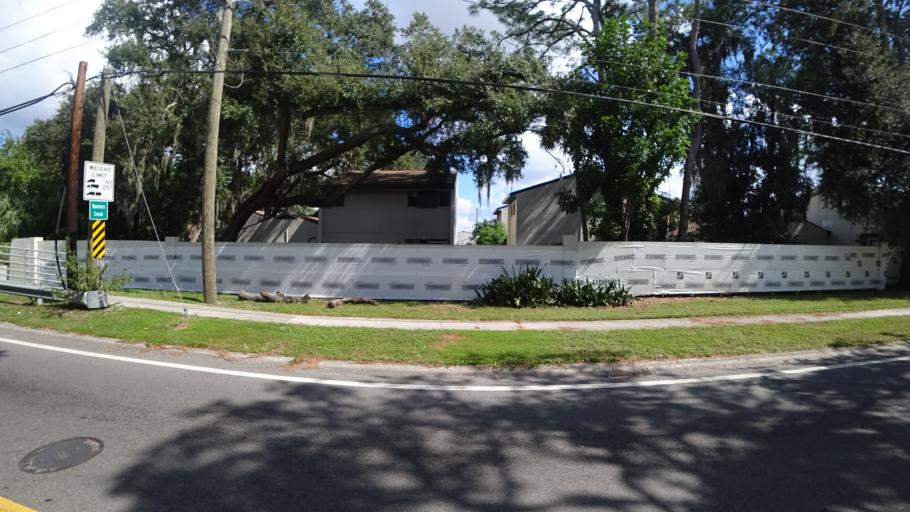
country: US
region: Florida
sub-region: Manatee County
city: Whitfield
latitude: 27.4193
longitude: -82.5550
